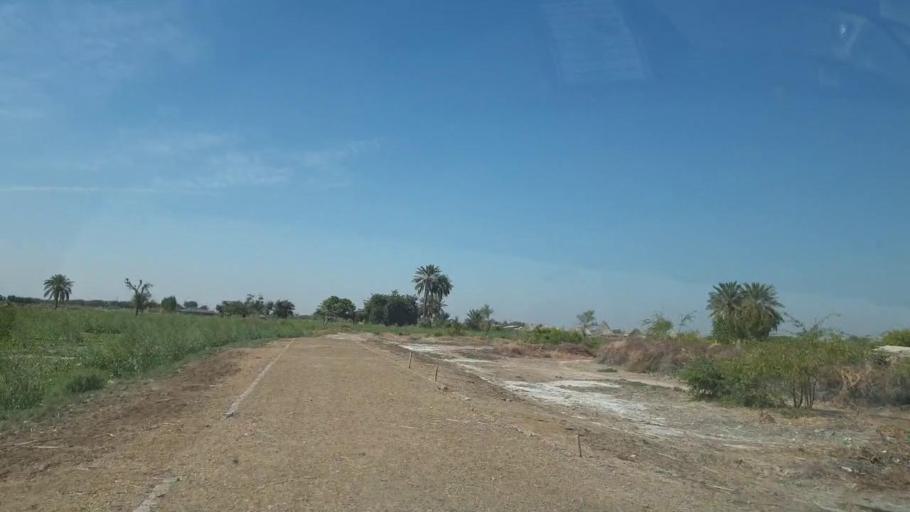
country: PK
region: Sindh
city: Pithoro
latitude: 25.6351
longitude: 69.2448
